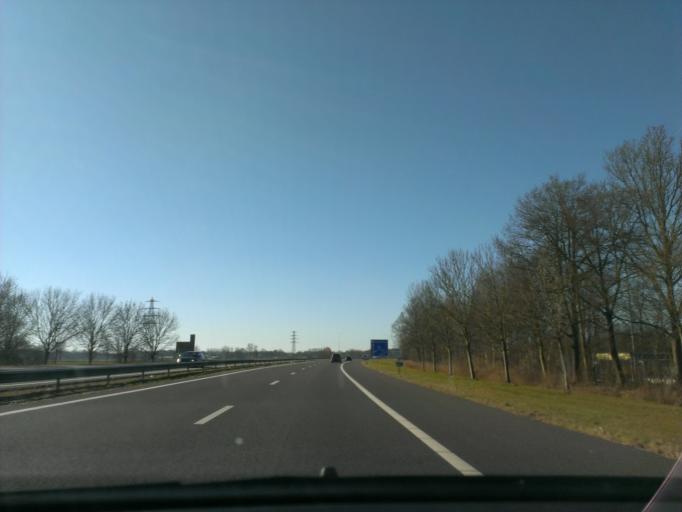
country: NL
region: Drenthe
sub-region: Gemeente Meppel
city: Meppel
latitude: 52.6872
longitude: 6.2044
